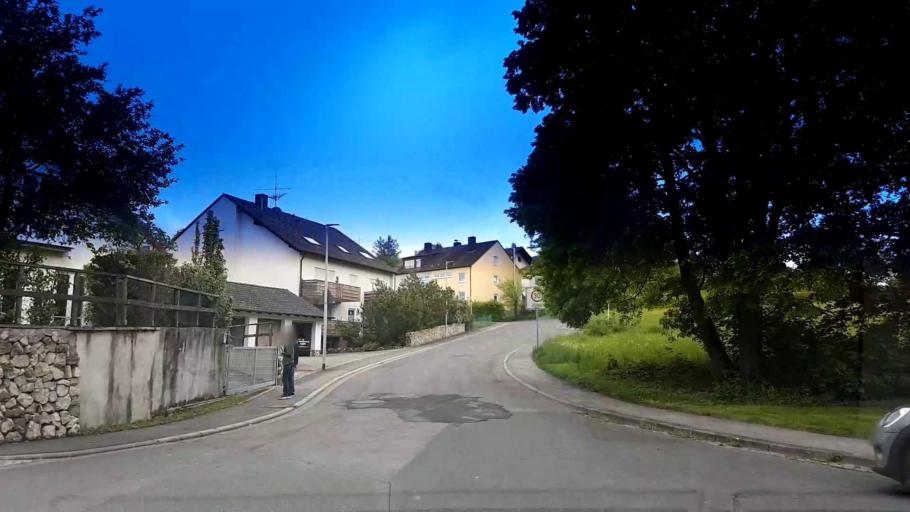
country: DE
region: Bavaria
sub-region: Upper Franconia
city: Bischberg
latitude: 49.9003
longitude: 10.8549
